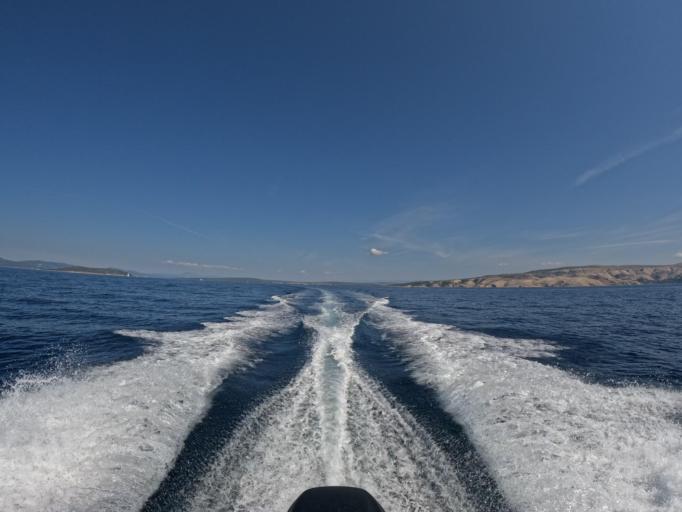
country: HR
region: Primorsko-Goranska
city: Punat
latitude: 44.9272
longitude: 14.6193
